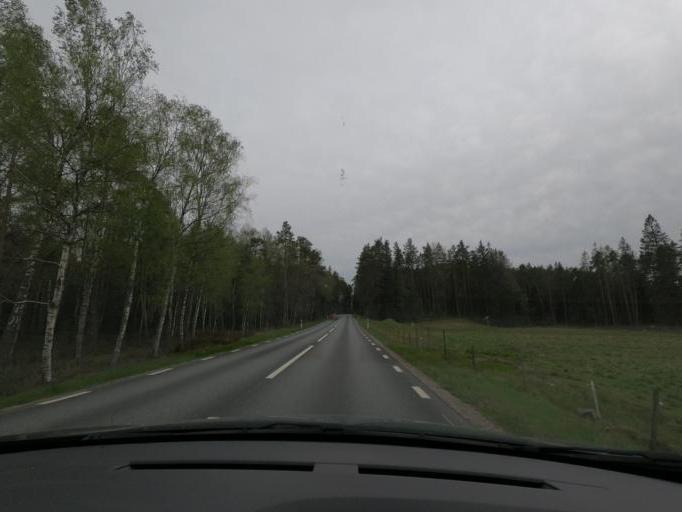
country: SE
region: Joenkoeping
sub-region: Varnamo Kommun
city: Bredaryd
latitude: 57.1975
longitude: 13.7624
